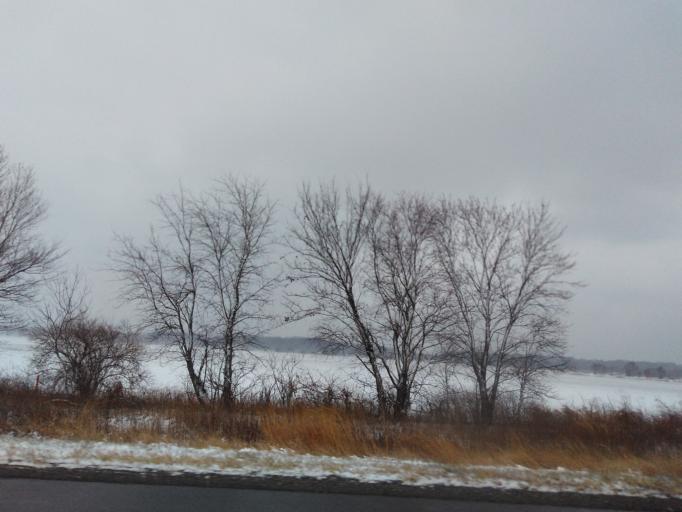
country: US
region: Illinois
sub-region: Saint Clair County
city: Caseyville
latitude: 38.6516
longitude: -90.0349
